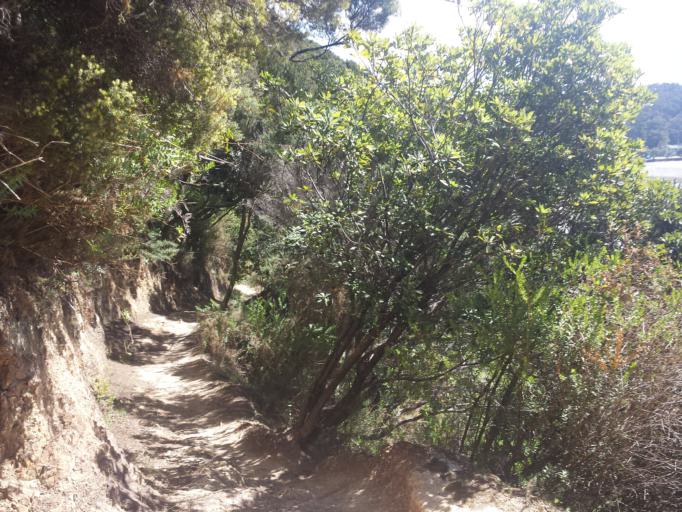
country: NZ
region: Northland
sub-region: Far North District
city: Paihia
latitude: -35.3022
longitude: 174.1072
